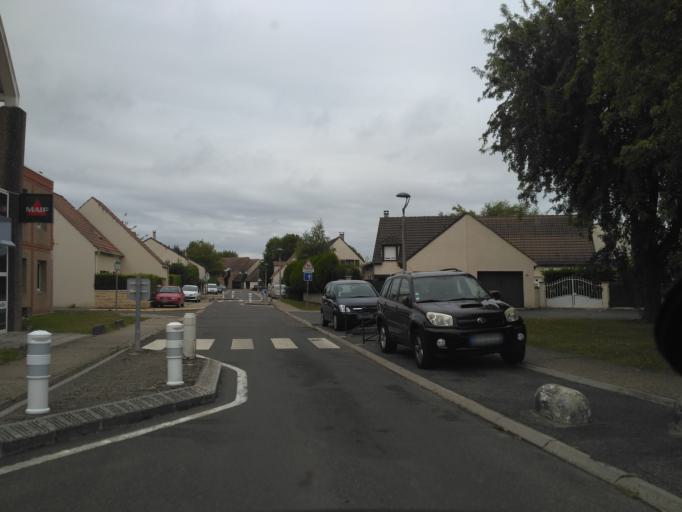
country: FR
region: Ile-de-France
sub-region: Departement de Seine-et-Marne
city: Vert-Saint-Denis
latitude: 48.5611
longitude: 2.6259
